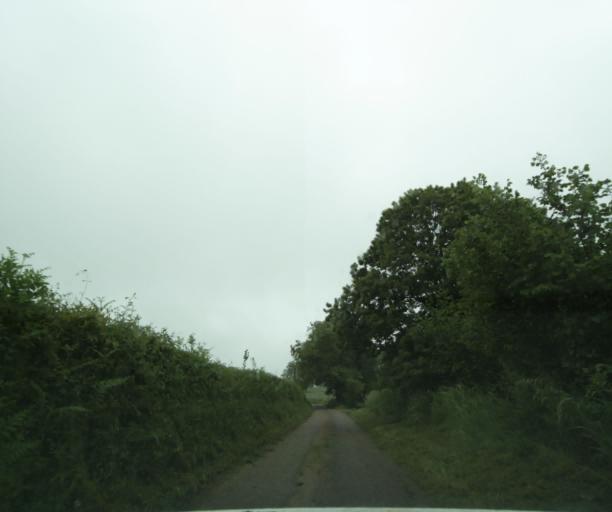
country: FR
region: Bourgogne
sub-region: Departement de Saone-et-Loire
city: Charolles
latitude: 46.4076
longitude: 4.3875
